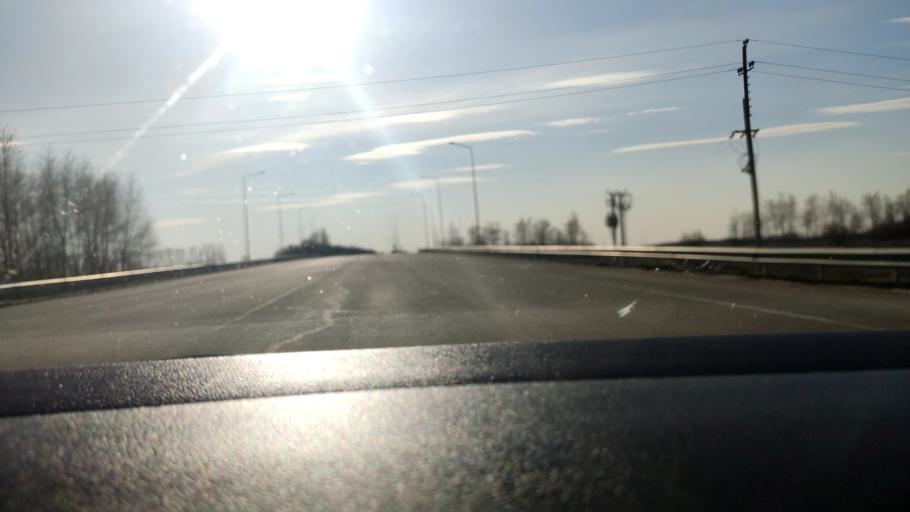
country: RU
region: Voronezj
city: Kolodeznyy
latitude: 51.3397
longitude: 39.0278
